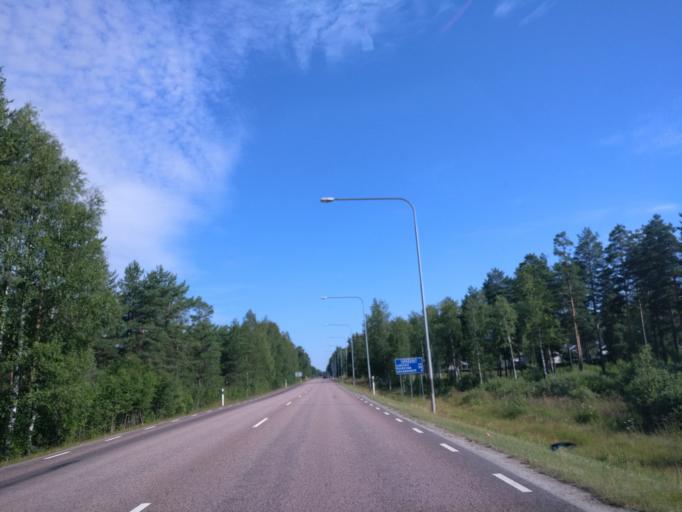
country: SE
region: Vaermland
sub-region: Hagfors Kommun
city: Hagfors
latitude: 60.0452
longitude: 13.7037
